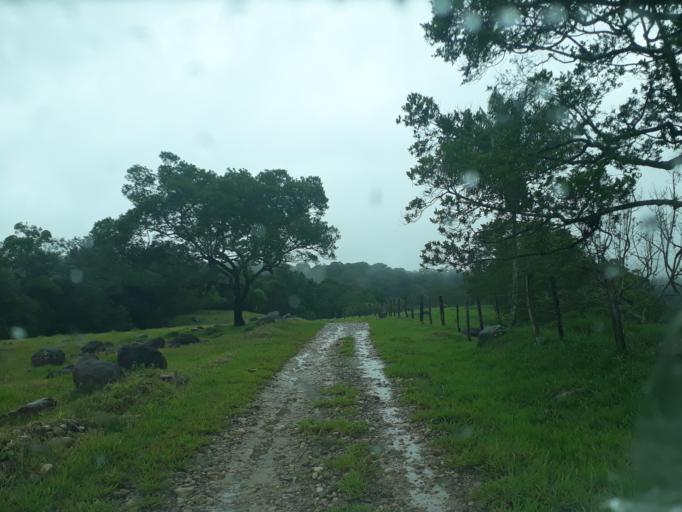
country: CO
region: Cundinamarca
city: Medina
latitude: 4.5307
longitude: -73.3692
